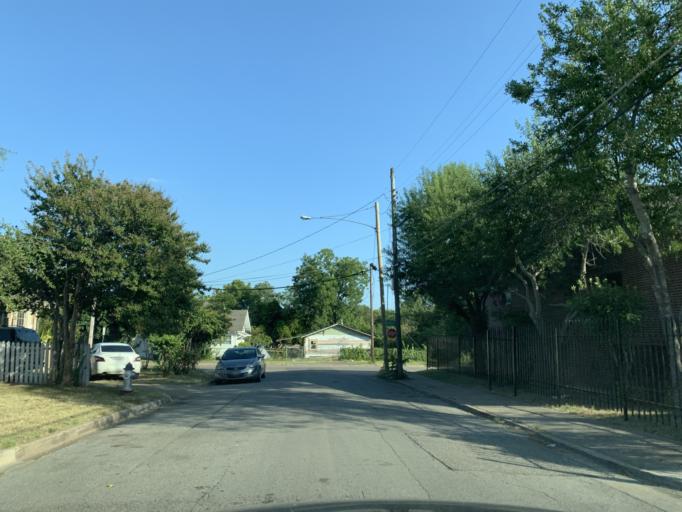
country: US
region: Texas
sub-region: Dallas County
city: Dallas
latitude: 32.7007
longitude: -96.7955
